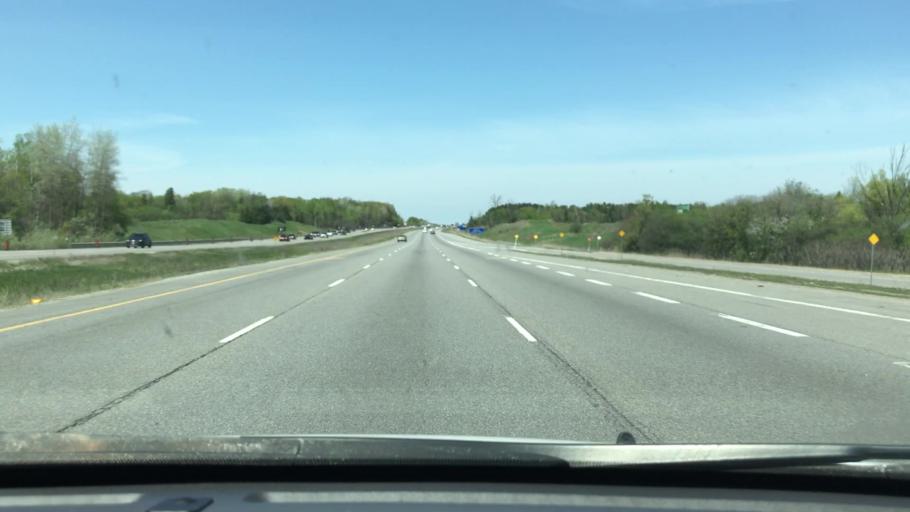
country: CA
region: Ontario
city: Newmarket
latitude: 43.9804
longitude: -79.3932
